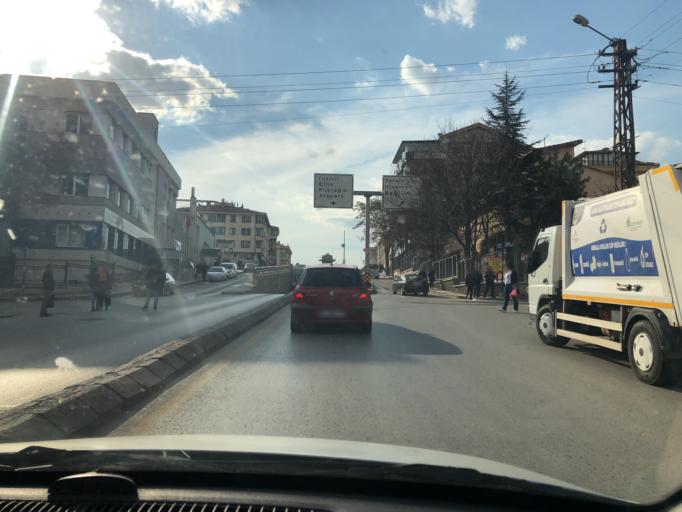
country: TR
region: Ankara
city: Ankara
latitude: 39.9845
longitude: 32.8605
